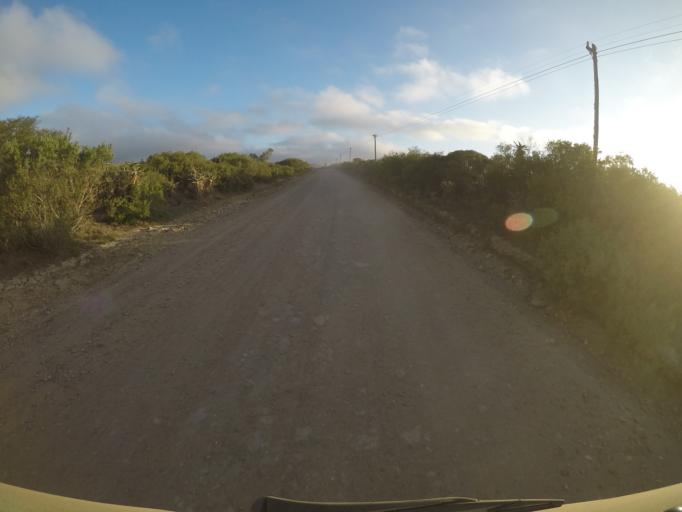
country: ZA
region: Western Cape
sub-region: Eden District Municipality
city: Mossel Bay
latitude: -34.1115
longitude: 22.0539
